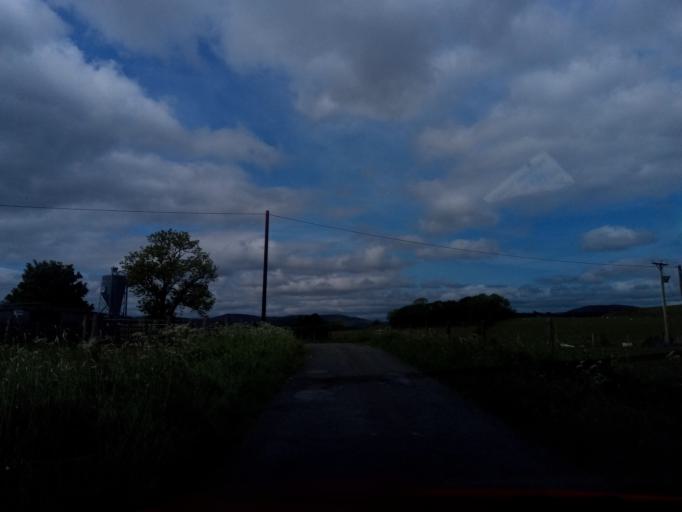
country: GB
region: Scotland
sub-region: The Scottish Borders
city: Selkirk
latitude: 55.5301
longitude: -2.8530
